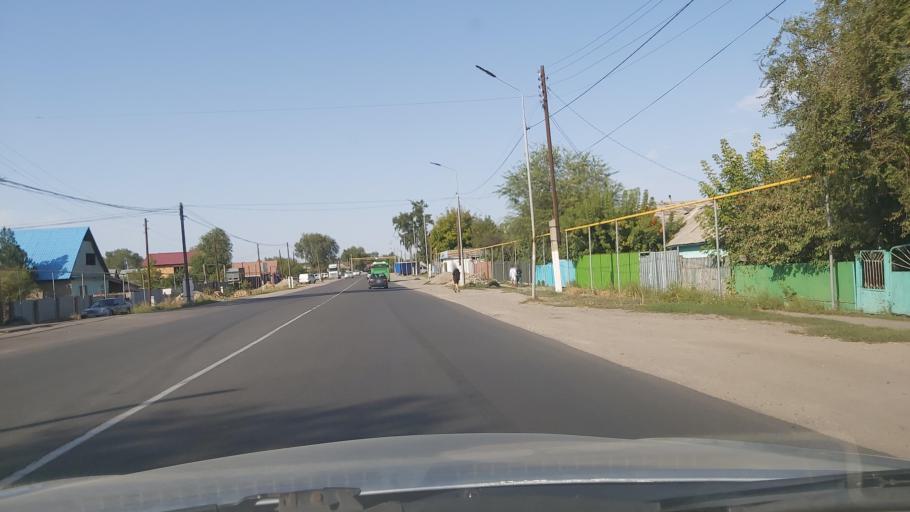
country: KZ
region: Almaty Oblysy
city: Energeticheskiy
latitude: 43.4915
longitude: 77.0350
